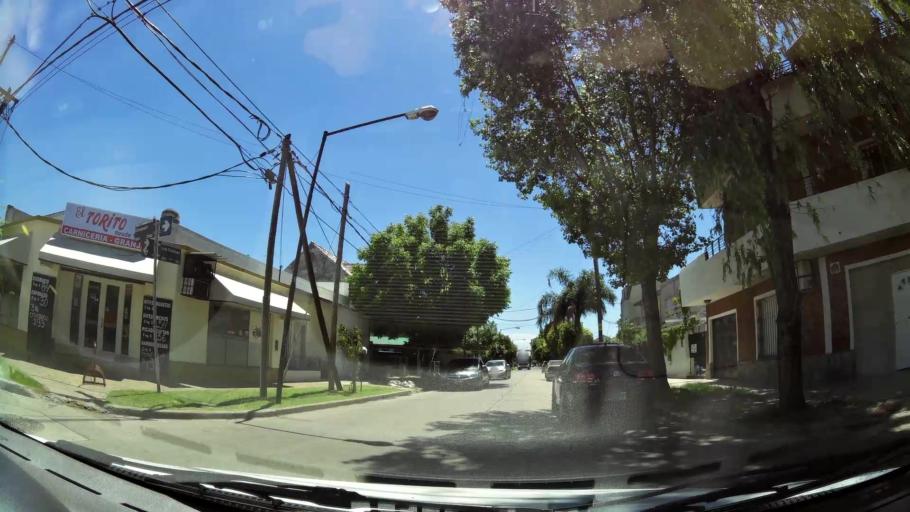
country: AR
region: Buenos Aires
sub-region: Partido de Vicente Lopez
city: Olivos
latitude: -34.5142
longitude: -58.5350
